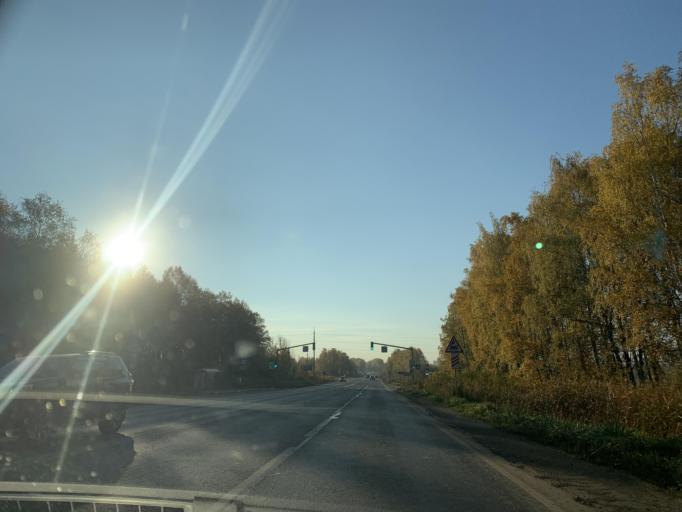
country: RU
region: Jaroslavl
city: Konstantinovskiy
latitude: 57.7358
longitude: 39.7336
